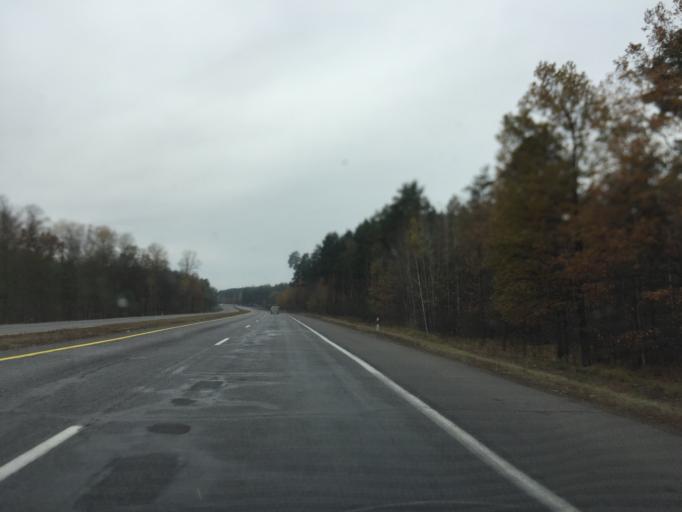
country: BY
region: Gomel
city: Horad Rechytsa
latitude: 52.3598
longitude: 30.6593
